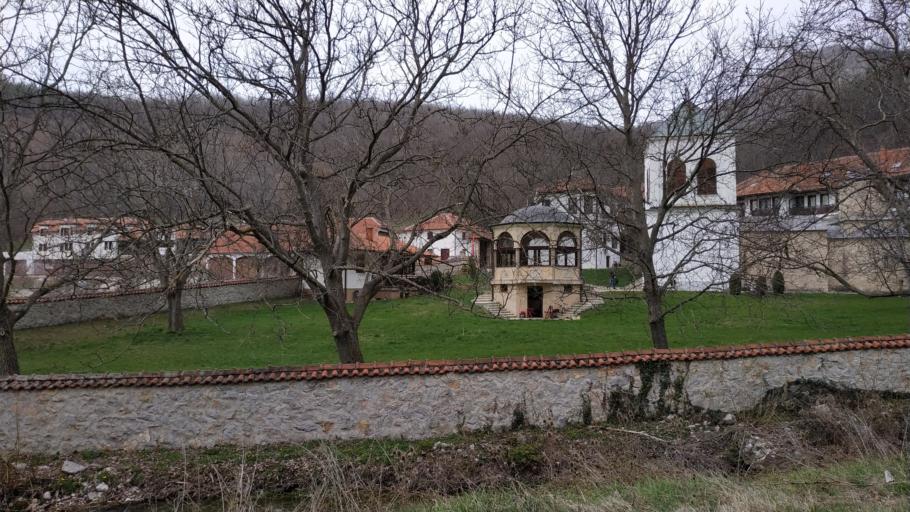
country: RS
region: Central Serbia
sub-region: Zajecarski Okrug
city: Soko Banja
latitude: 43.5610
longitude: 21.8344
